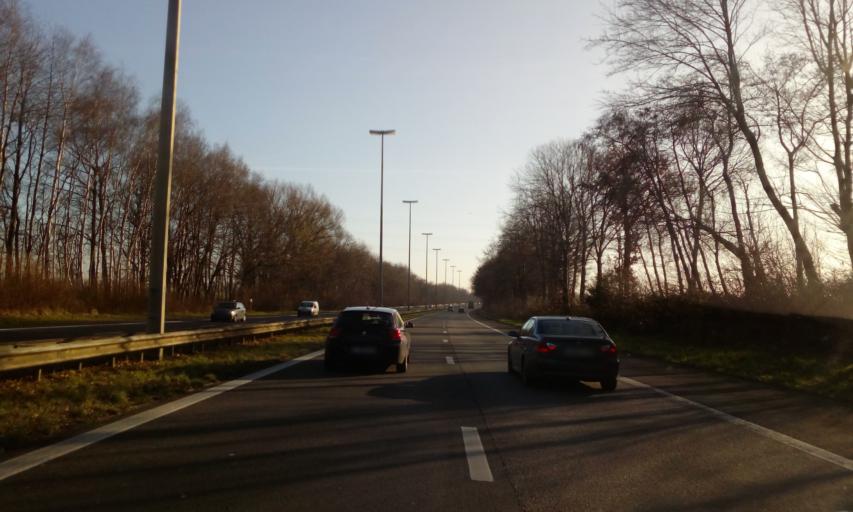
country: BE
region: Wallonia
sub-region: Province du Hainaut
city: Pont-a-Celles
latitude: 50.5539
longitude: 4.3640
